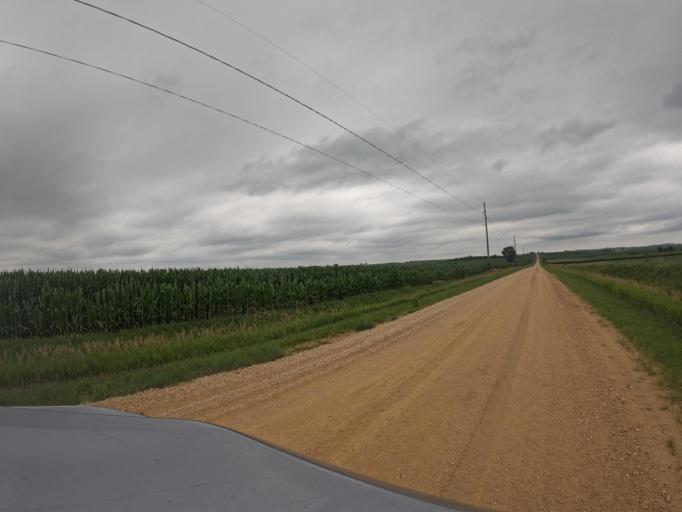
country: US
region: Iowa
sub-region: Jackson County
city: Maquoketa
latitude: 41.9544
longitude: -90.5870
